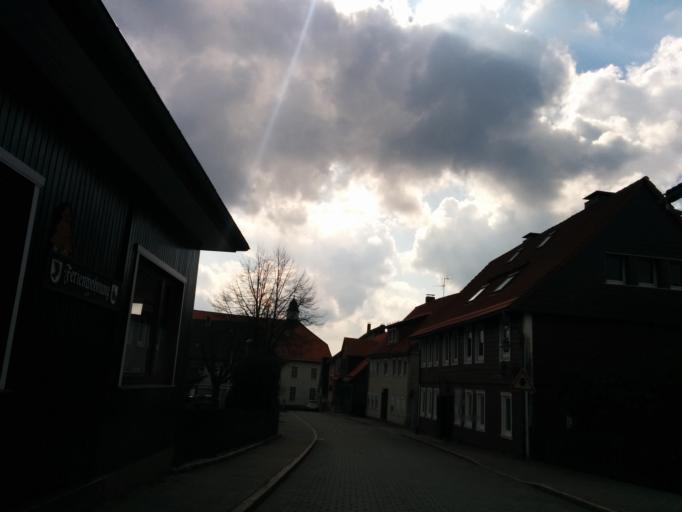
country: DE
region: Lower Saxony
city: Sankt Andreasberg
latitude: 51.7105
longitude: 10.5201
